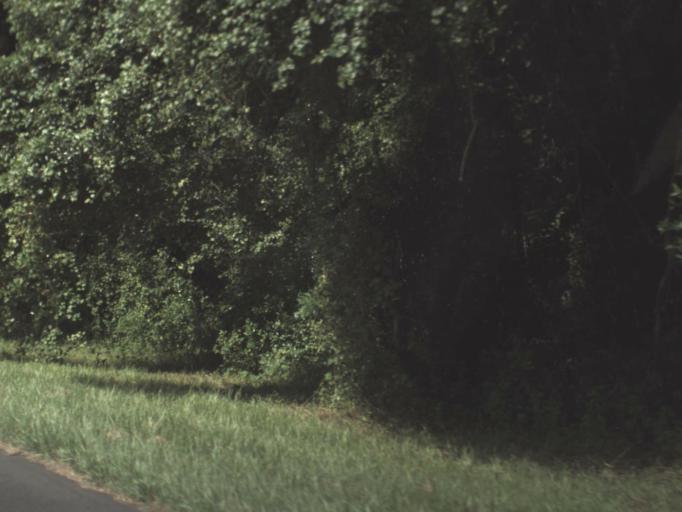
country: US
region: Florida
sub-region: Citrus County
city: Floral City
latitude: 28.7221
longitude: -82.3069
